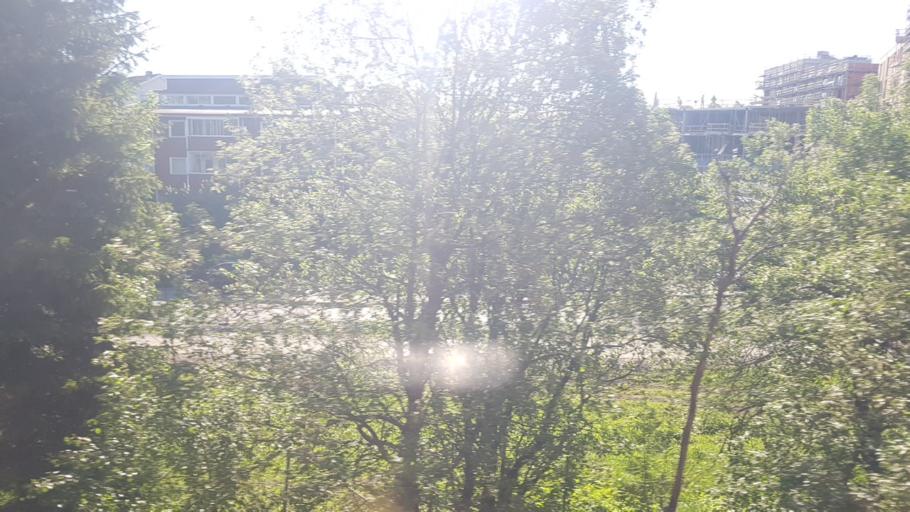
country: NO
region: Sor-Trondelag
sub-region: Trondheim
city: Trondheim
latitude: 63.3583
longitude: 10.3600
